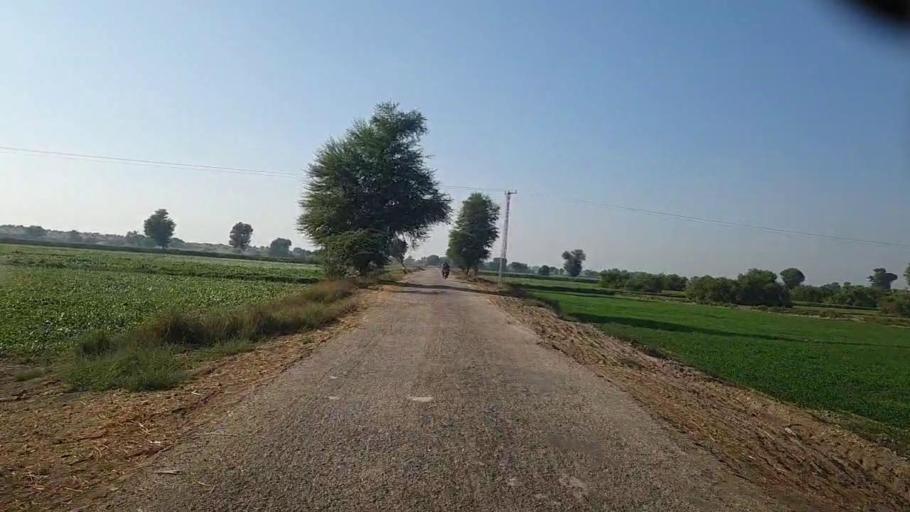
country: PK
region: Sindh
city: Darya Khan Marri
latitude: 26.6856
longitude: 68.3533
